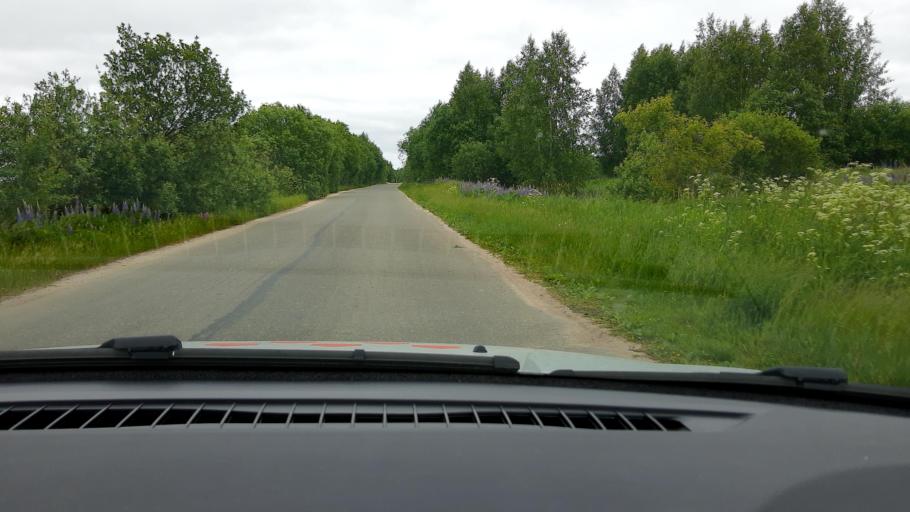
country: RU
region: Nizjnij Novgorod
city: Sitniki
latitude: 56.5058
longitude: 44.0879
